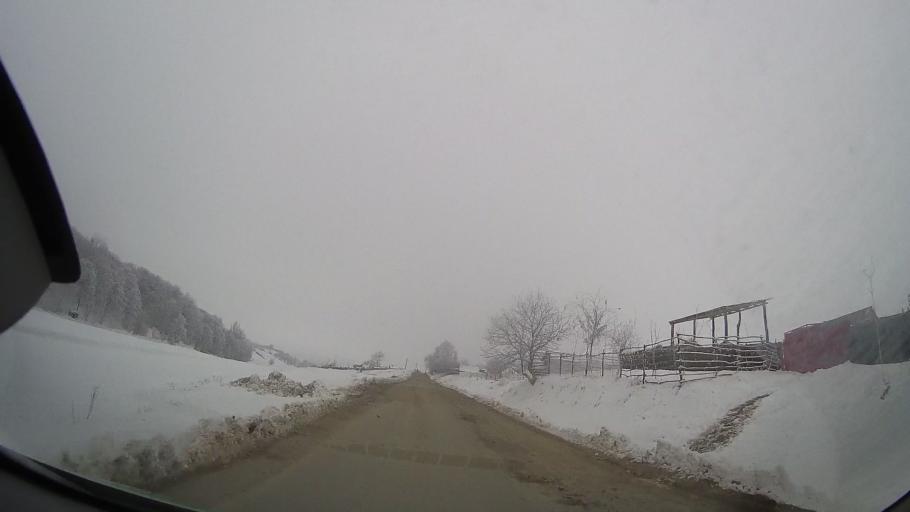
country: RO
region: Neamt
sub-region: Comuna Pancesti
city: Pancesti
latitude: 46.9125
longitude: 27.1599
